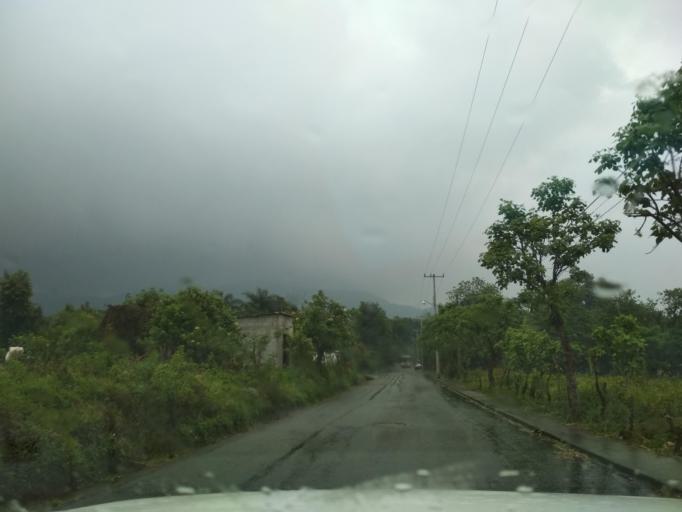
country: MX
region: Veracruz
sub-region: Mariano Escobedo
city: Chicola
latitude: 18.9012
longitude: -97.1188
